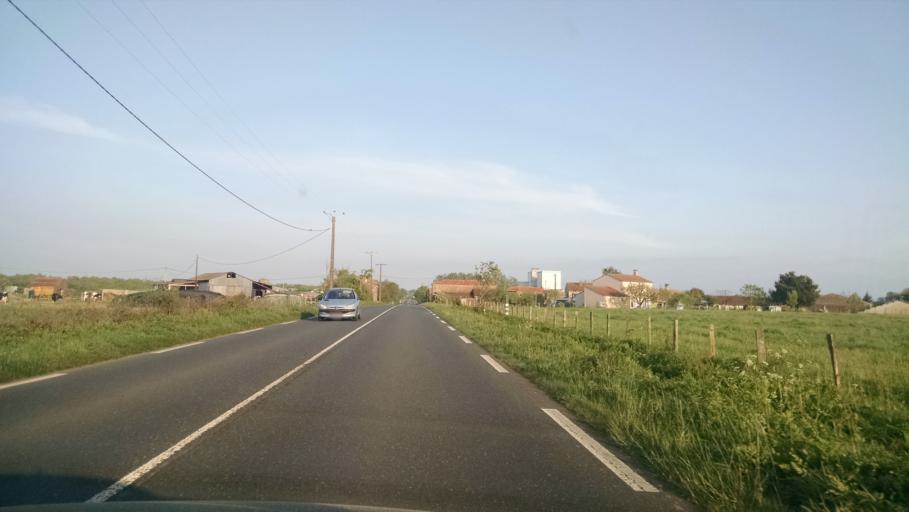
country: FR
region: Pays de la Loire
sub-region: Departement de la Loire-Atlantique
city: Boussay
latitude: 47.0629
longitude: -1.1940
